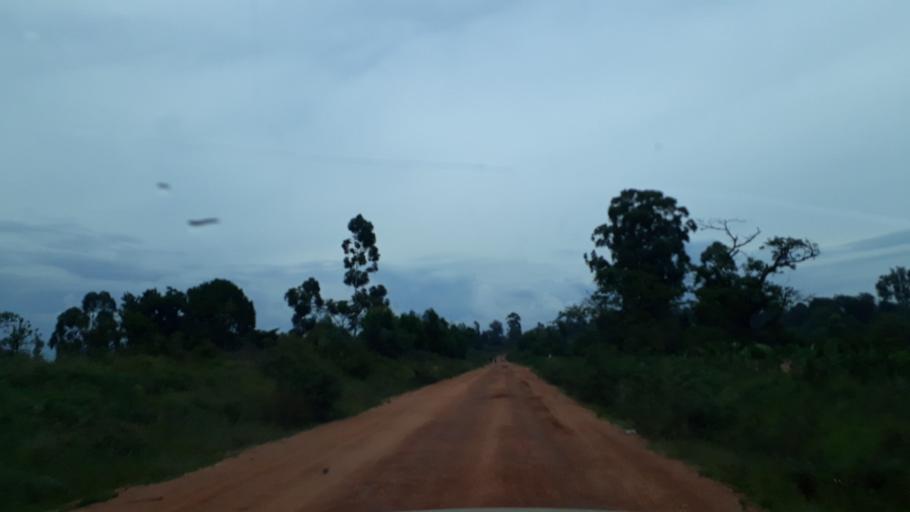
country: UG
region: Northern Region
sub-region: Zombo District
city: Paidha
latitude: 2.2079
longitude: 30.7524
